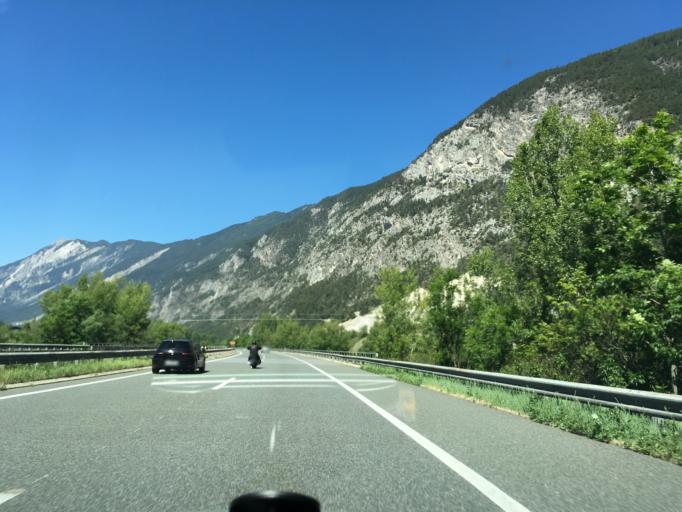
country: AT
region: Tyrol
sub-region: Politischer Bezirk Imst
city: Silz
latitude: 47.2735
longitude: 10.9418
